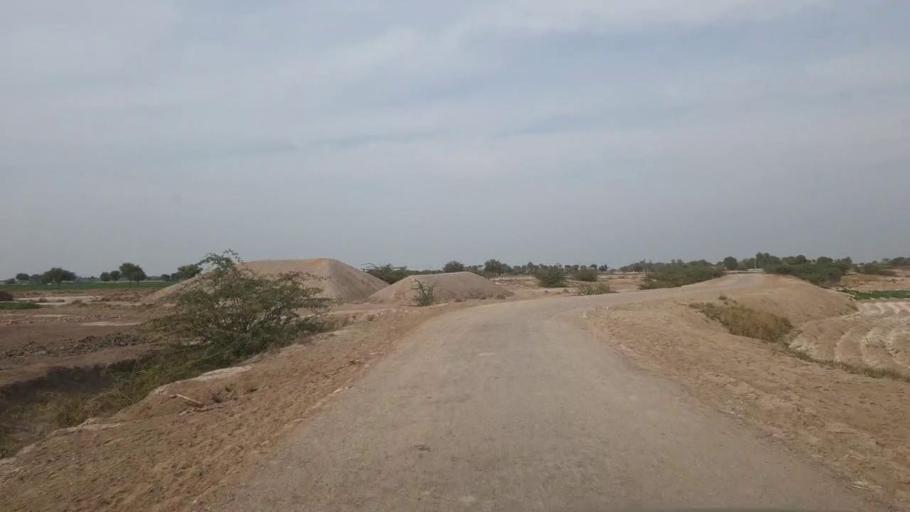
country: PK
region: Sindh
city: Shahpur Chakar
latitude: 26.1033
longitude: 68.5045
